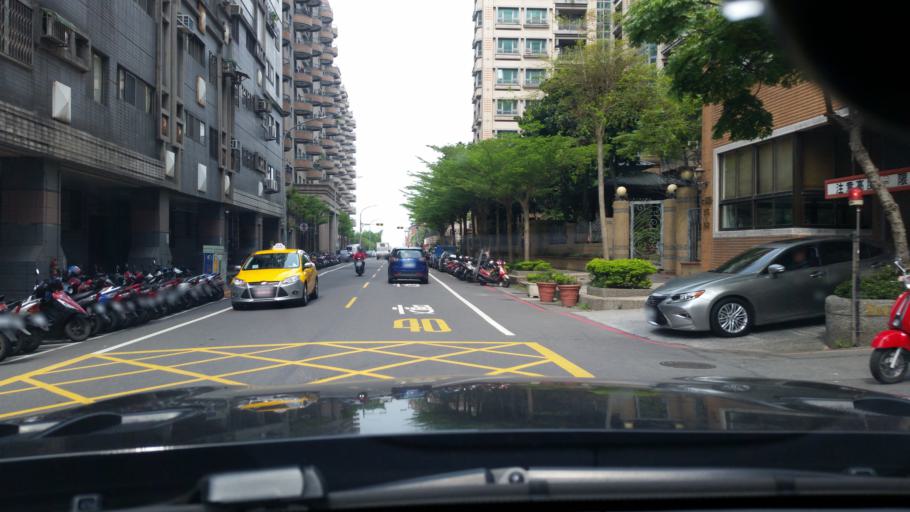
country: TW
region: Taiwan
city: Taoyuan City
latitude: 25.0615
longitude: 121.2976
